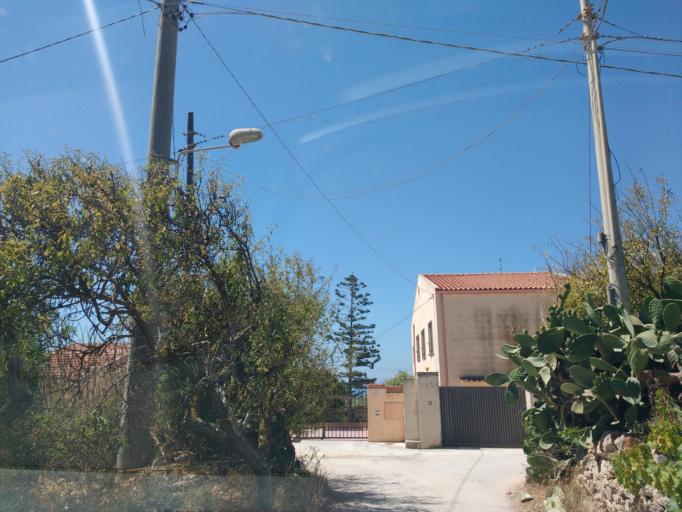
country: IT
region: Sicily
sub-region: Ragusa
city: Cava d'Aliga
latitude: 36.7241
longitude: 14.6916
